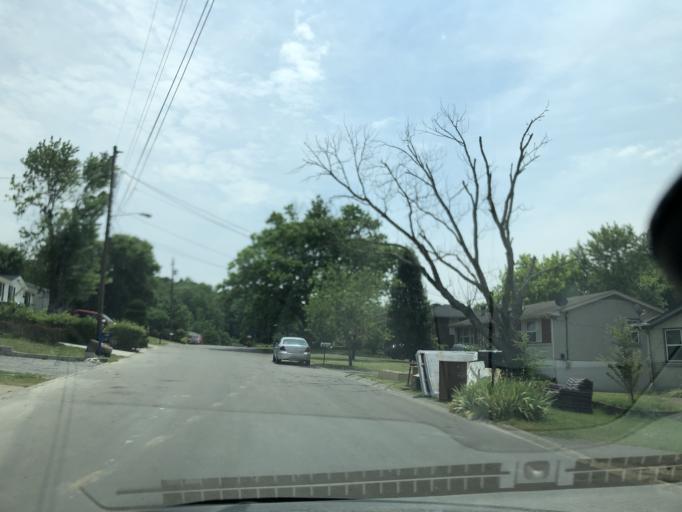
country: US
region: Tennessee
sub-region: Rutherford County
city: La Vergne
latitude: 36.0708
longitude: -86.6736
